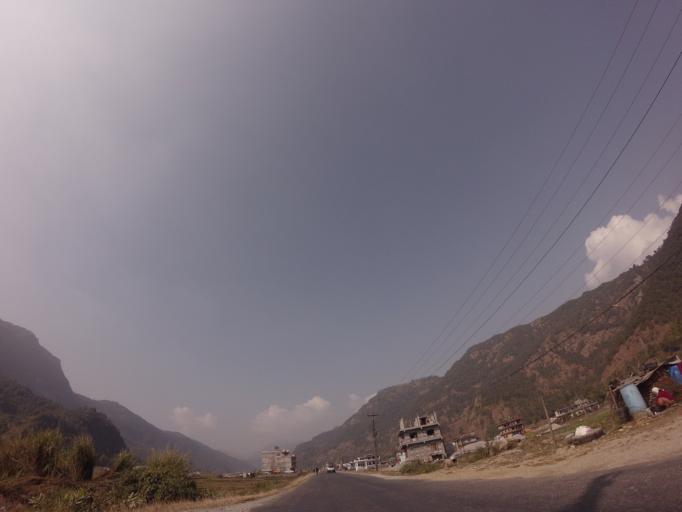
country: NP
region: Western Region
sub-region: Gandaki Zone
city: Pokhara
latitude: 28.2826
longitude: 83.9240
